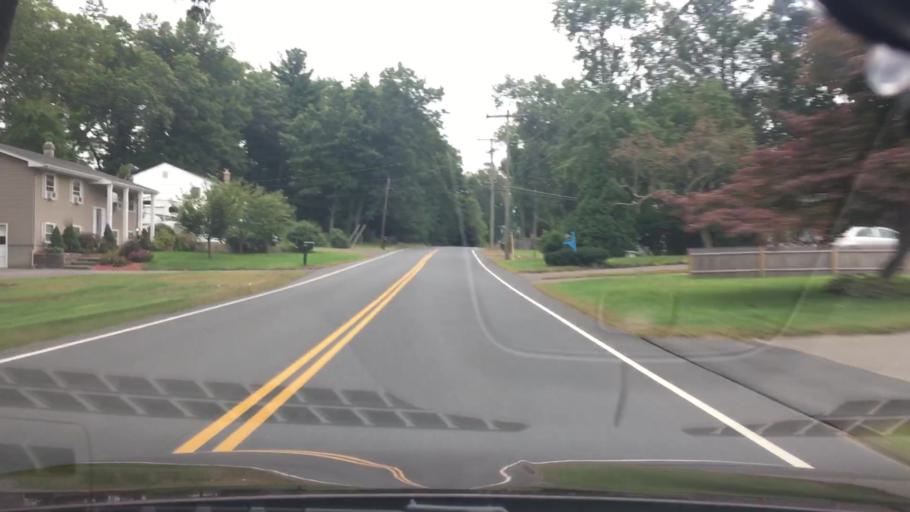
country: US
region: Connecticut
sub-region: Hartford County
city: Sherwood Manor
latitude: 42.0265
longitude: -72.5599
